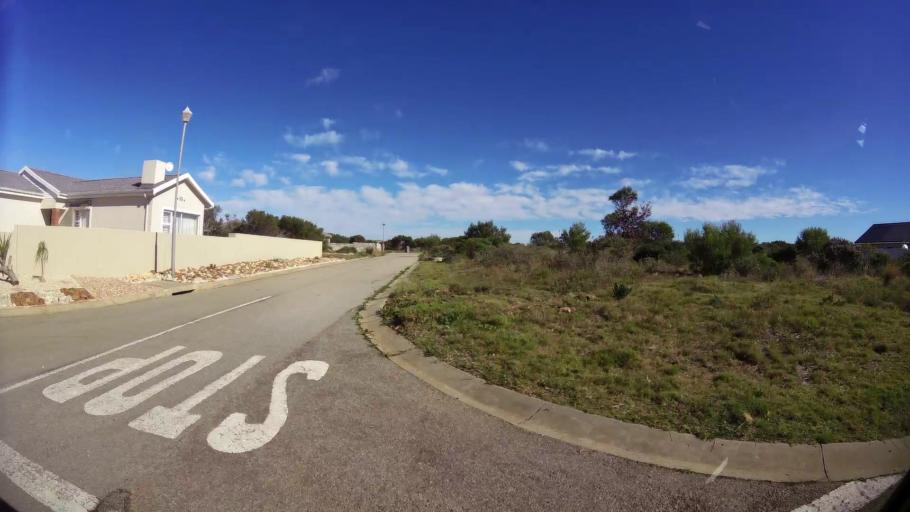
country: ZA
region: Eastern Cape
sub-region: Cacadu District Municipality
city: Jeffrey's Bay
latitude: -34.0336
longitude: 24.9085
